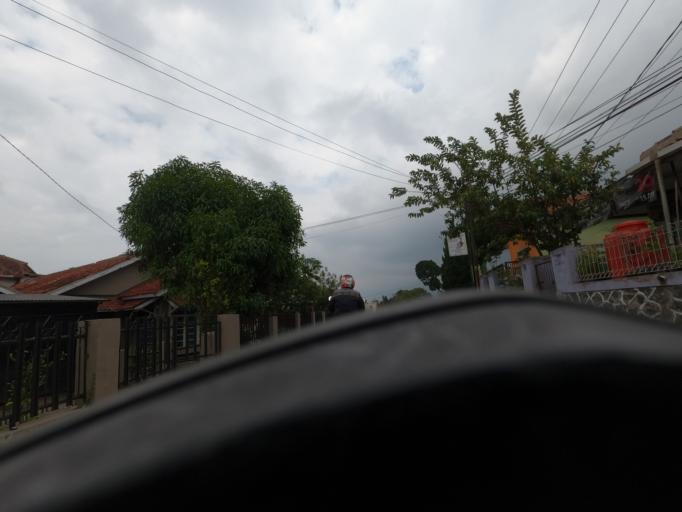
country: ID
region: West Java
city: Cimahi
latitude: -6.8166
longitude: 107.5467
